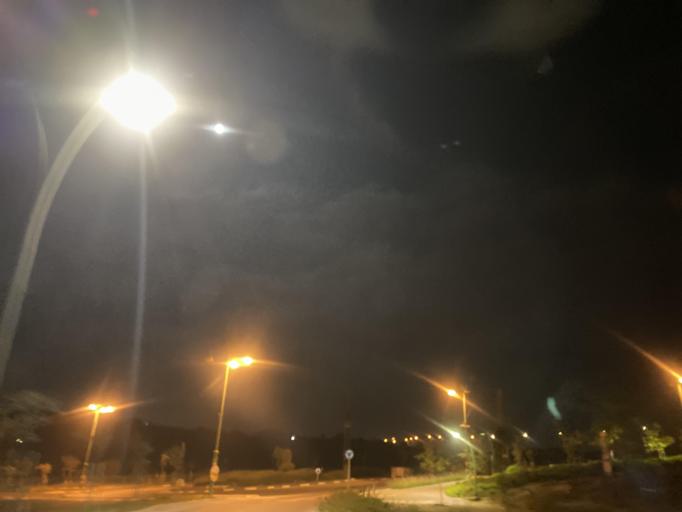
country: IL
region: Haifa
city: Daliyat el Karmil
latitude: 32.6348
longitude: 35.0780
